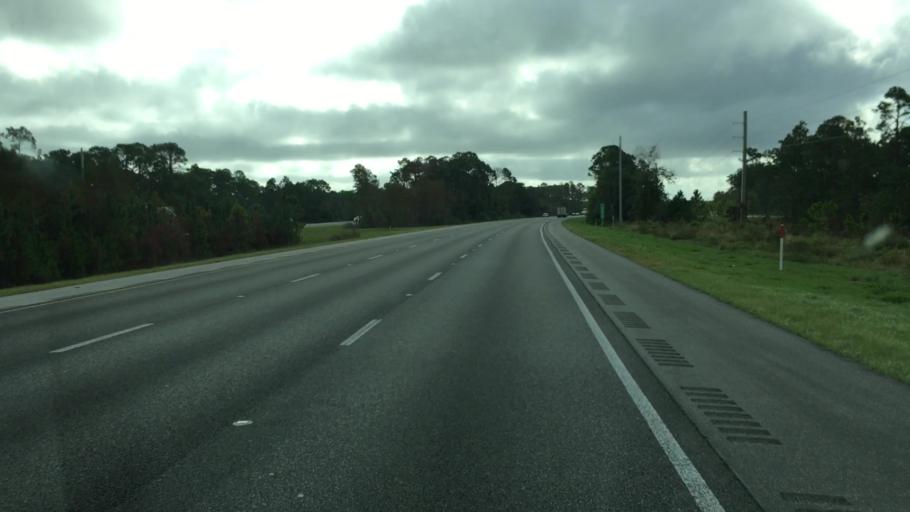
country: US
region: Florida
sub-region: Volusia County
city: Samsula-Spruce Creek
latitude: 29.0699
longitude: -81.0112
